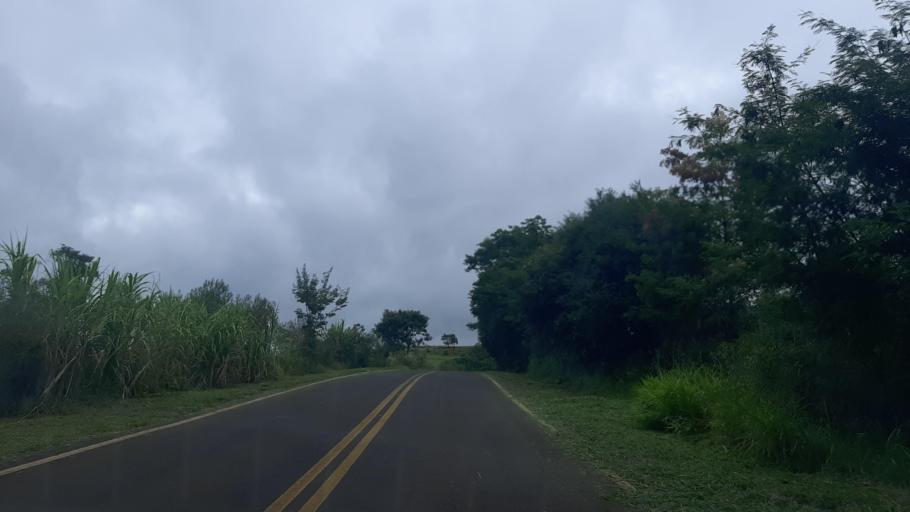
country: BR
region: Parana
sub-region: Ampere
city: Ampere
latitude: -25.9413
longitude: -53.4625
